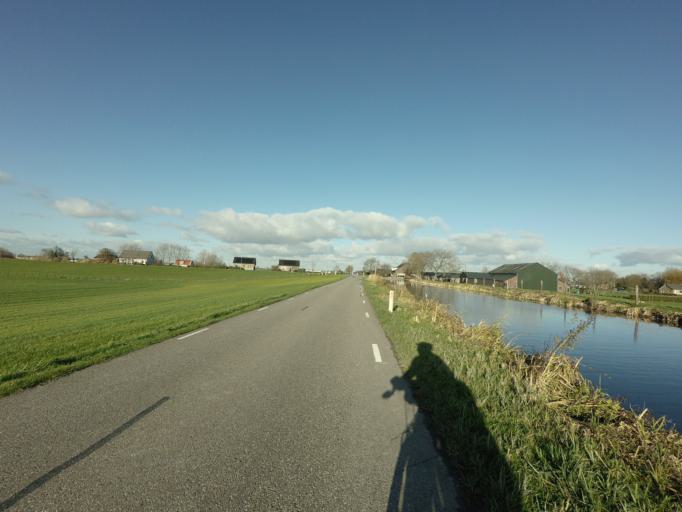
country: NL
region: South Holland
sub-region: Gemeente Nieuwkoop
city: Nieuwkoop
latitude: 52.2027
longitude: 4.7692
